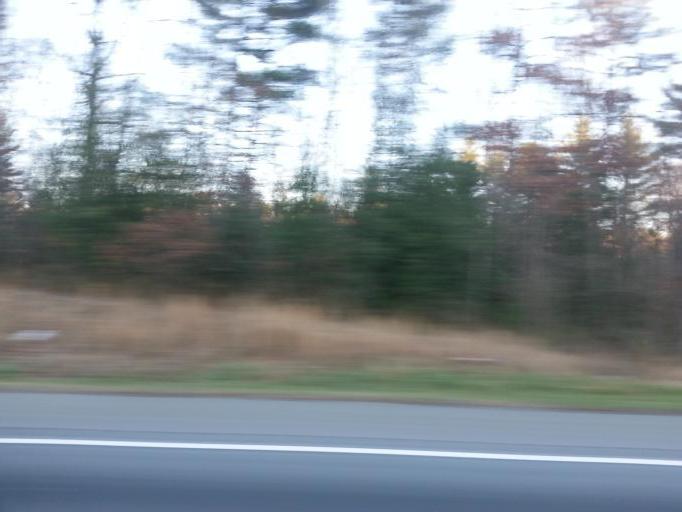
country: US
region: North Carolina
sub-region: Buncombe County
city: Bent Creek
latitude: 35.5238
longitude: -82.5962
